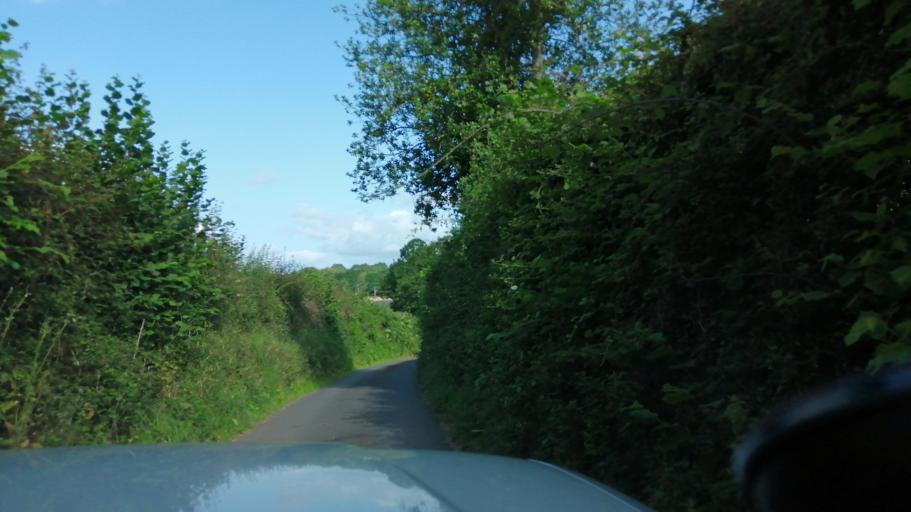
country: GB
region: England
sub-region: Herefordshire
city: Kingstone
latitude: 52.0318
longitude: -2.8145
